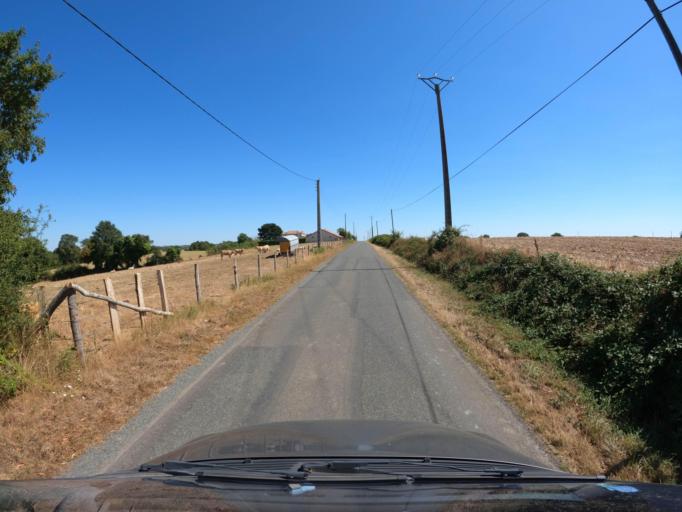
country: FR
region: Pays de la Loire
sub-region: Departement de Maine-et-Loire
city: Saint-Christophe-du-Bois
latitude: 47.0461
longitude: -0.9575
